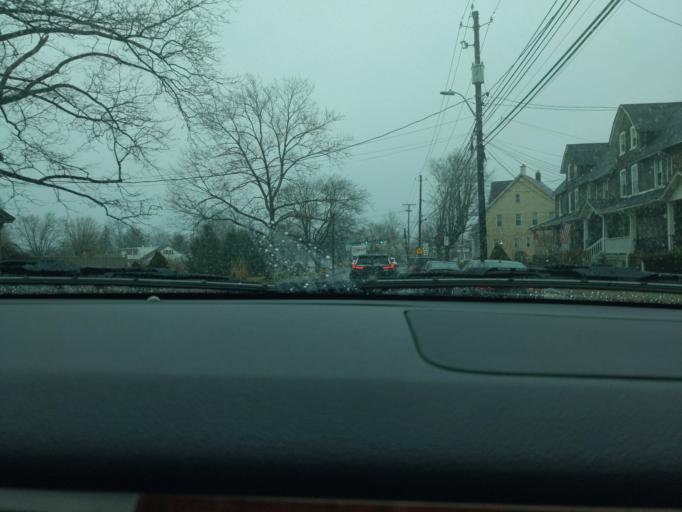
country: US
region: Pennsylvania
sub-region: Bucks County
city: Quakertown
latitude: 40.4389
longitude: -75.3251
